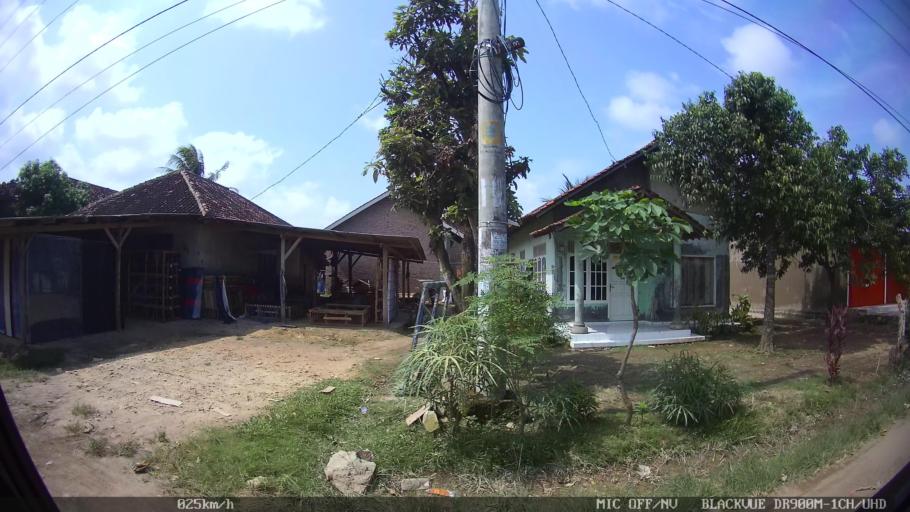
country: ID
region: Lampung
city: Kedaton
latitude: -5.3415
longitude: 105.2842
